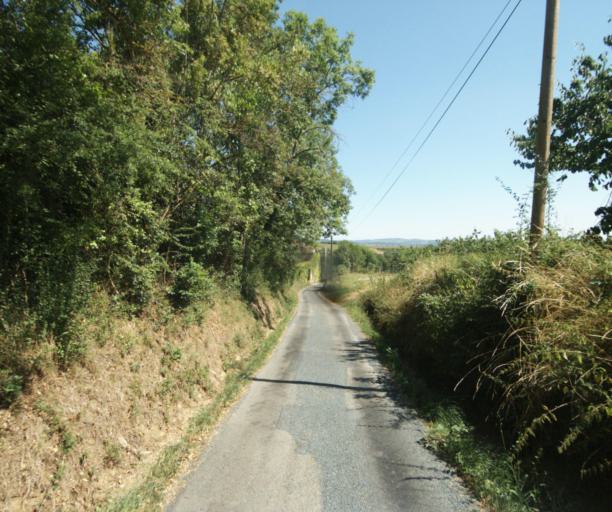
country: FR
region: Rhone-Alpes
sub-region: Departement du Rhone
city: Bessenay
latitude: 45.8004
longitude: 4.5494
